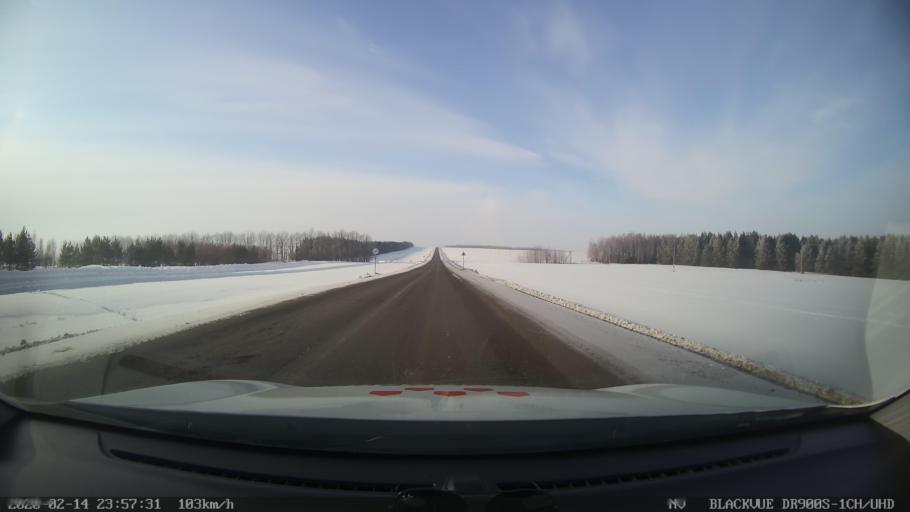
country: RU
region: Tatarstan
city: Kuybyshevskiy Zaton
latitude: 55.3346
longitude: 49.1075
